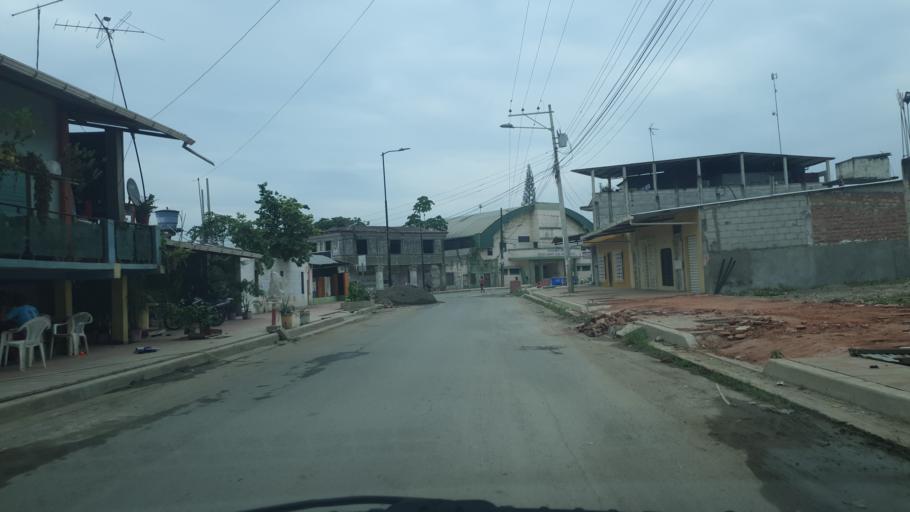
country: EC
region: El Oro
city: Pasaje
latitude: -3.3625
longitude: -79.8428
